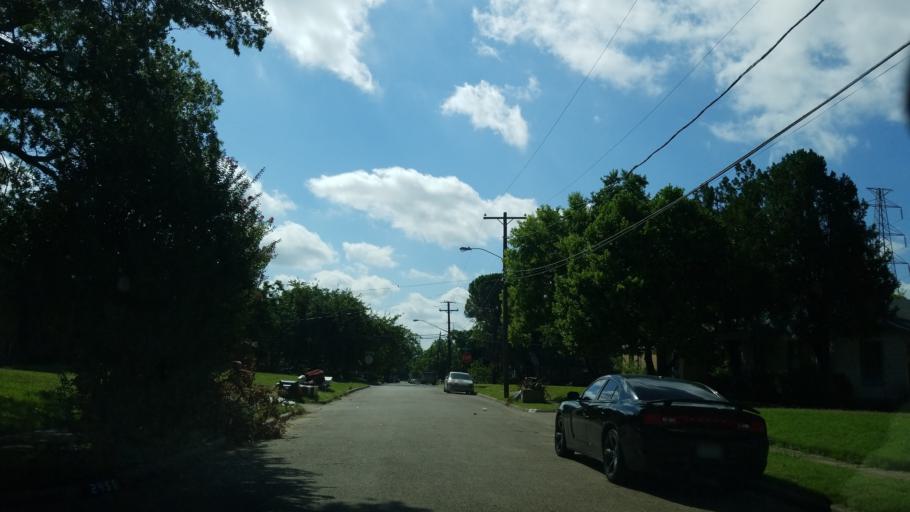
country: US
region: Texas
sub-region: Dallas County
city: Dallas
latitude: 32.7186
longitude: -96.7916
